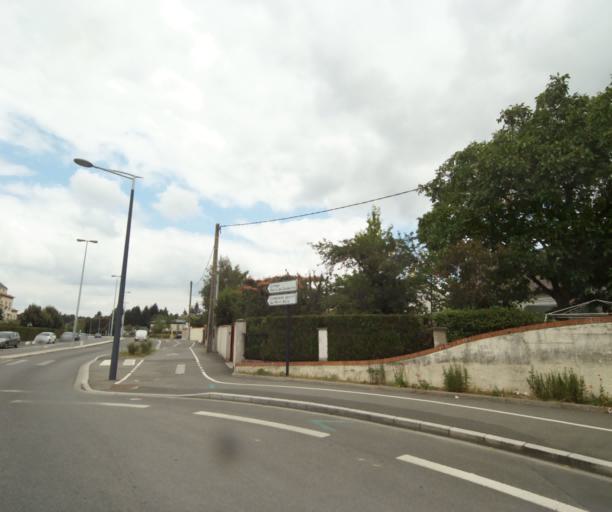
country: FR
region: Centre
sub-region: Departement du Loiret
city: Saint-Jean-de-Braye
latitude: 47.9118
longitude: 1.9781
